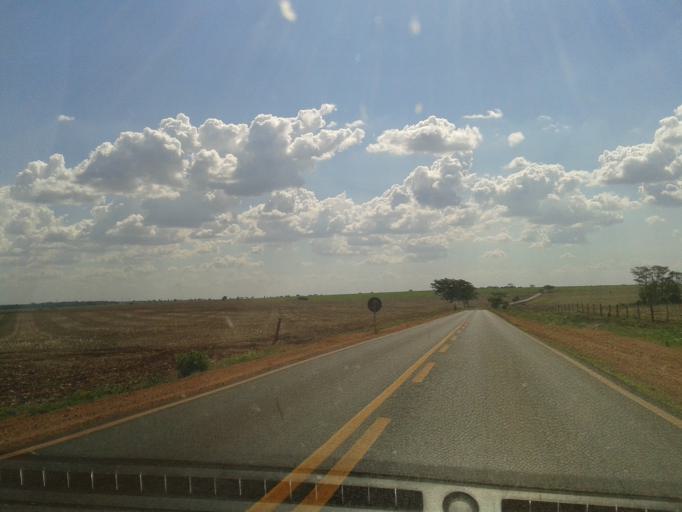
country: BR
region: Minas Gerais
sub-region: Capinopolis
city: Capinopolis
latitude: -18.6930
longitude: -49.4816
